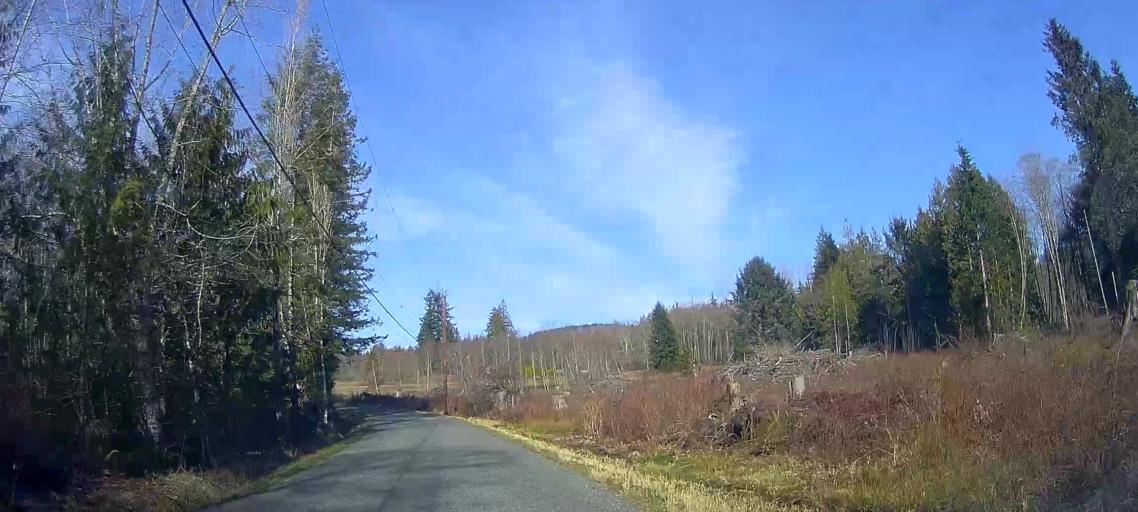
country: US
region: Washington
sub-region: Skagit County
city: Burlington
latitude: 48.5945
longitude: -122.3667
